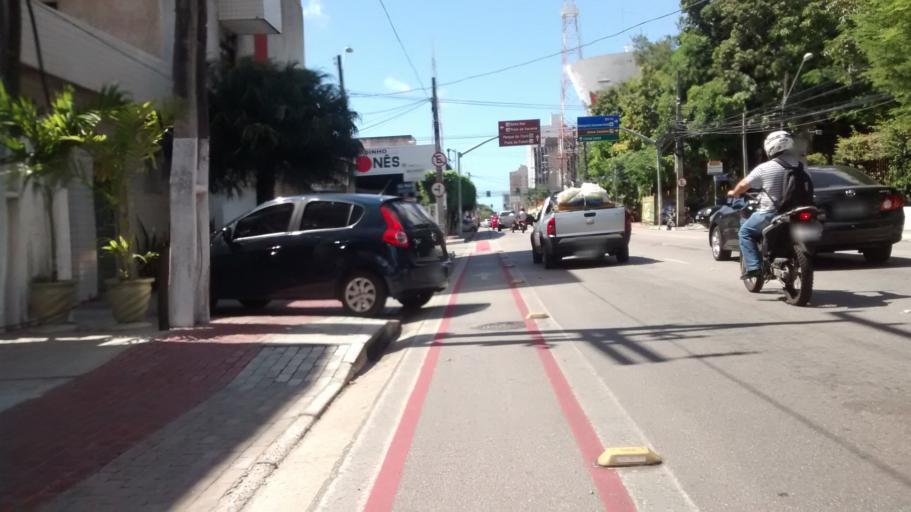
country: BR
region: Ceara
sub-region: Fortaleza
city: Fortaleza
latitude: -3.7453
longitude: -38.5028
